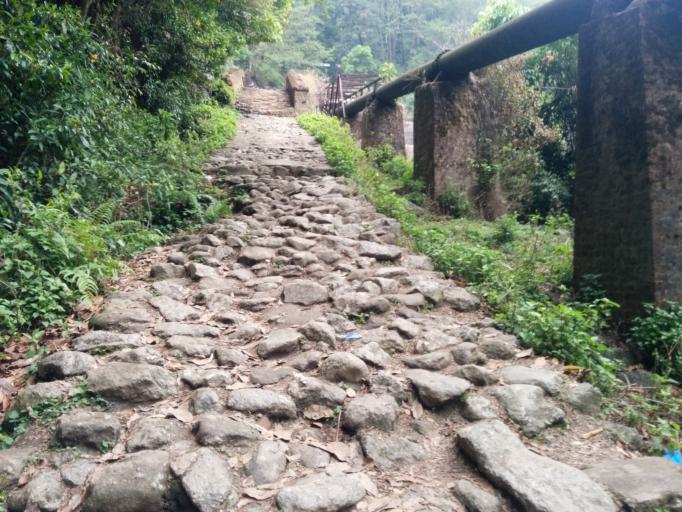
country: NP
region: Central Region
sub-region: Bagmati Zone
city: Bhaktapur
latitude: 27.7670
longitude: 85.4236
